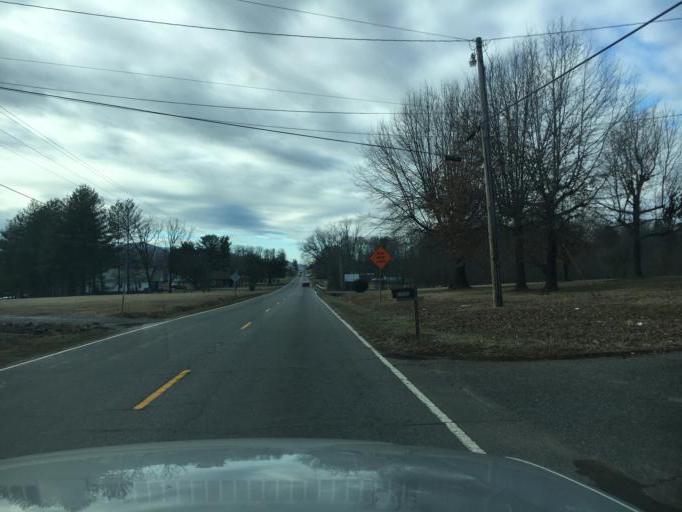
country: US
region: North Carolina
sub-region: Burke County
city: Salem
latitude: 35.6869
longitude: -81.7262
